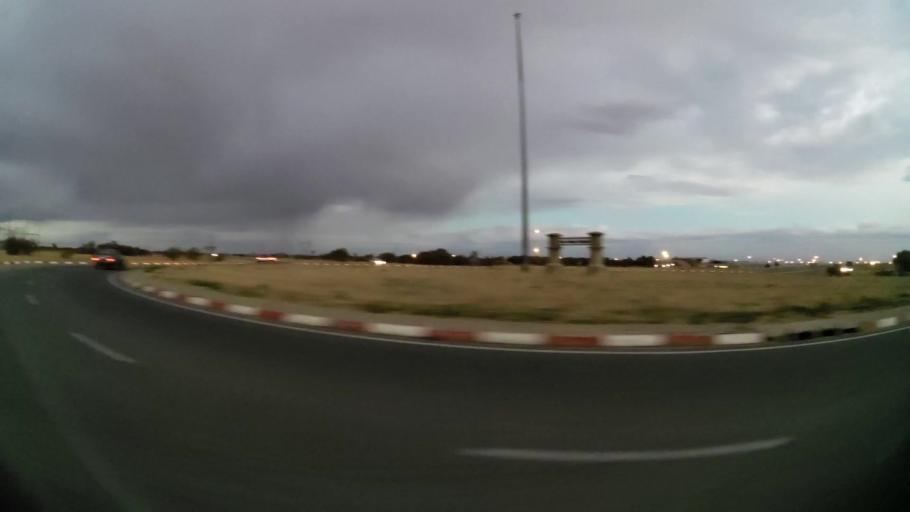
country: ZA
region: Orange Free State
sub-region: Lejweleputswa District Municipality
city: Welkom
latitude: -27.9489
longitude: 26.7966
